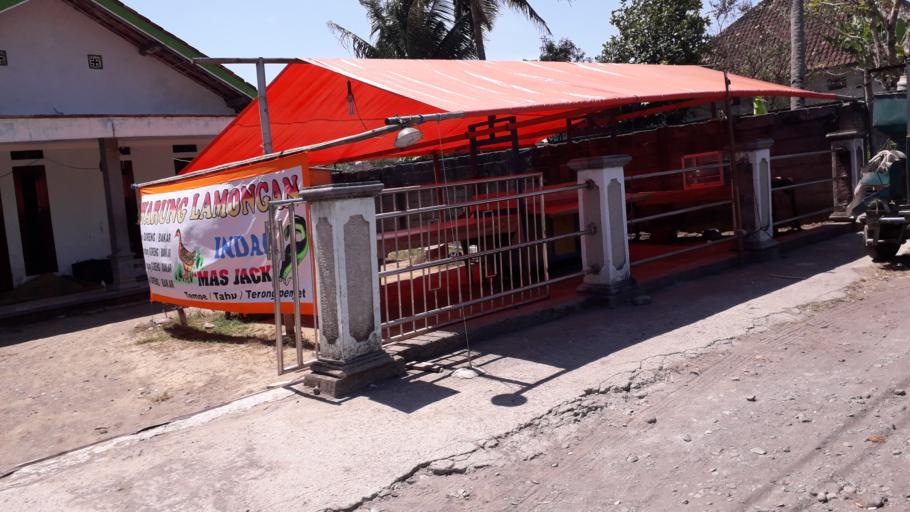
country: ID
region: Daerah Istimewa Yogyakarta
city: Pundong
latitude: -7.9810
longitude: 110.3168
